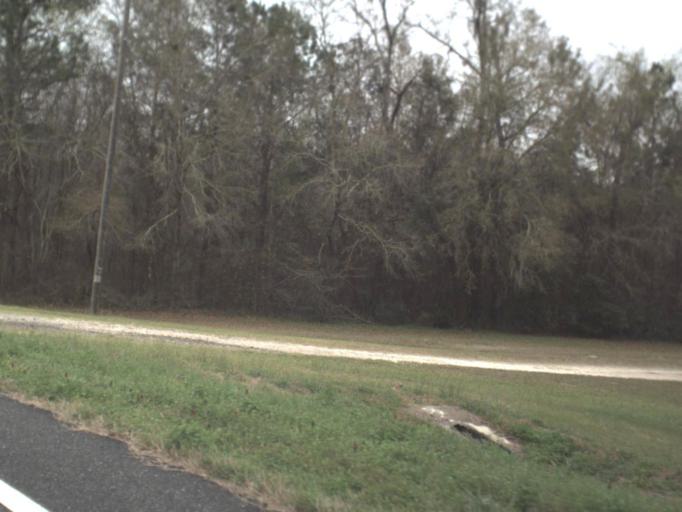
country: US
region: Florida
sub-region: Jefferson County
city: Monticello
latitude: 30.4100
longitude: -83.9623
